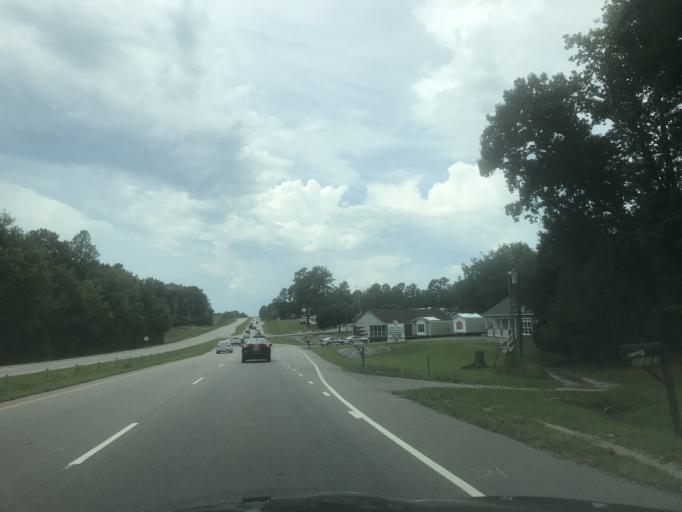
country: US
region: North Carolina
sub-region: Wake County
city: Garner
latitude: 35.6839
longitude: -78.5384
